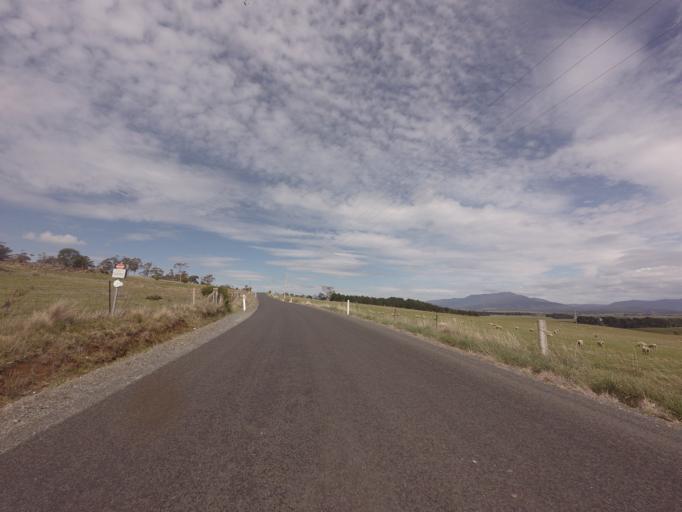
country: AU
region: Tasmania
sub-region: Northern Midlands
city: Longford
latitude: -41.7654
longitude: 147.2117
